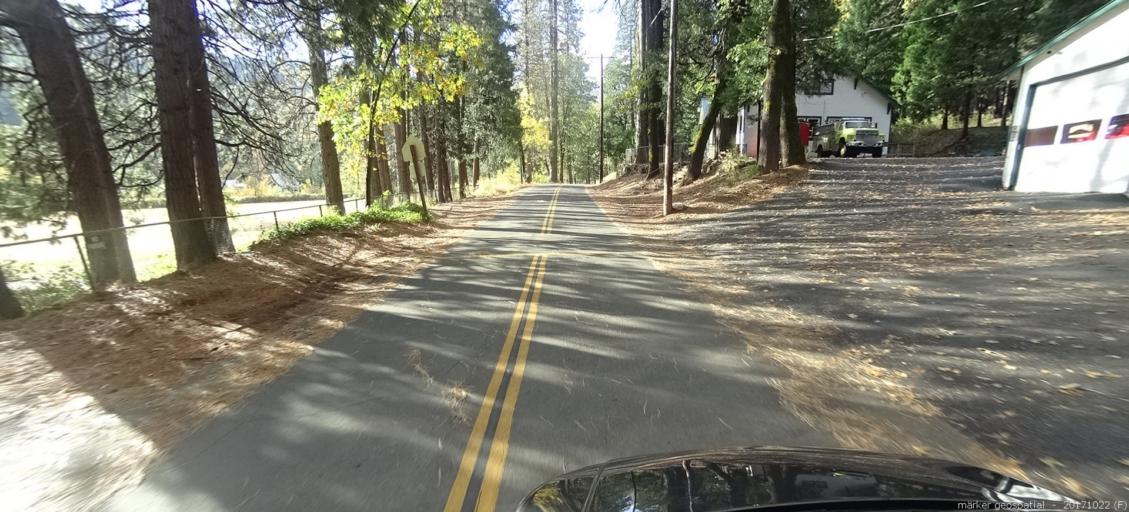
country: US
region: California
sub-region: Siskiyou County
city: Dunsmuir
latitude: 41.1427
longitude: -122.3170
